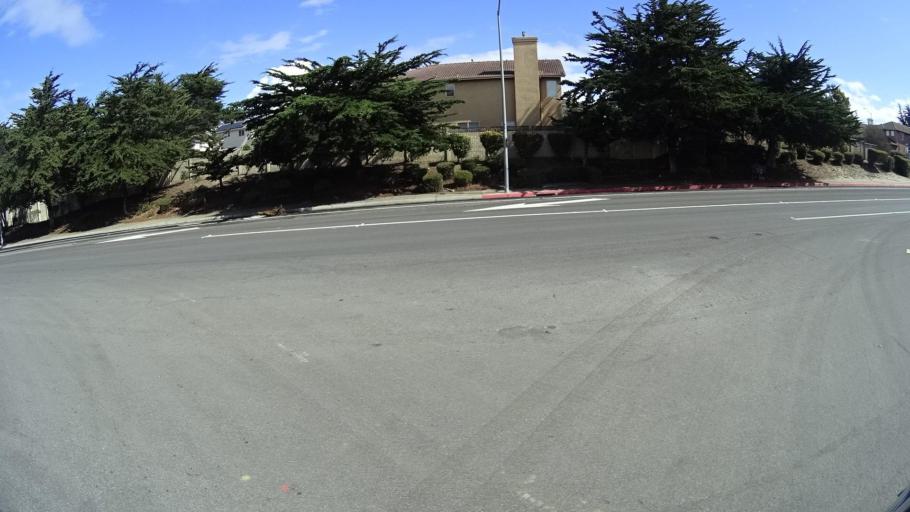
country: US
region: California
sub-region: Monterey County
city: Marina
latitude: 36.6946
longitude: -121.7996
